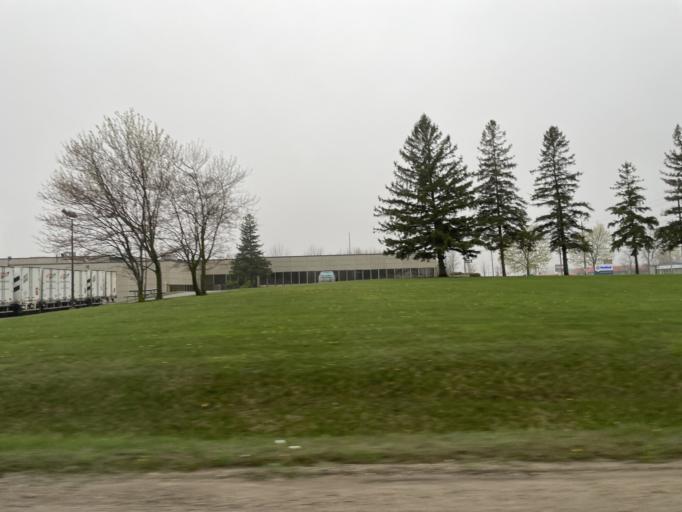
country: CA
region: Ontario
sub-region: Wellington County
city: Guelph
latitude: 43.5459
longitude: -80.3025
